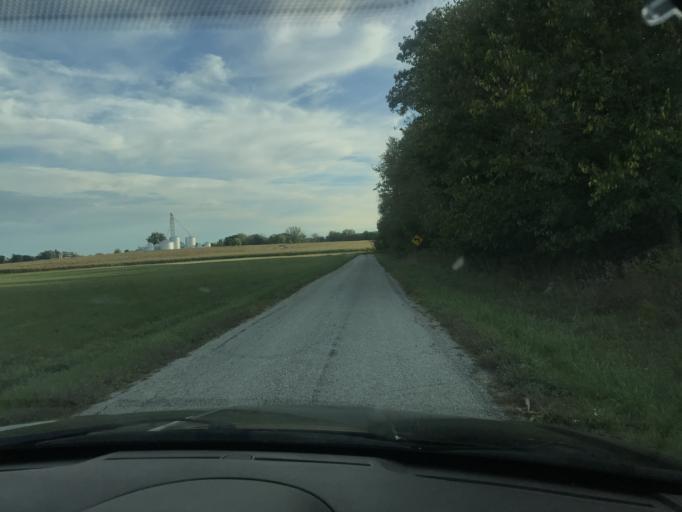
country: US
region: Ohio
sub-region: Logan County
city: West Liberty
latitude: 40.2045
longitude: -83.8091
